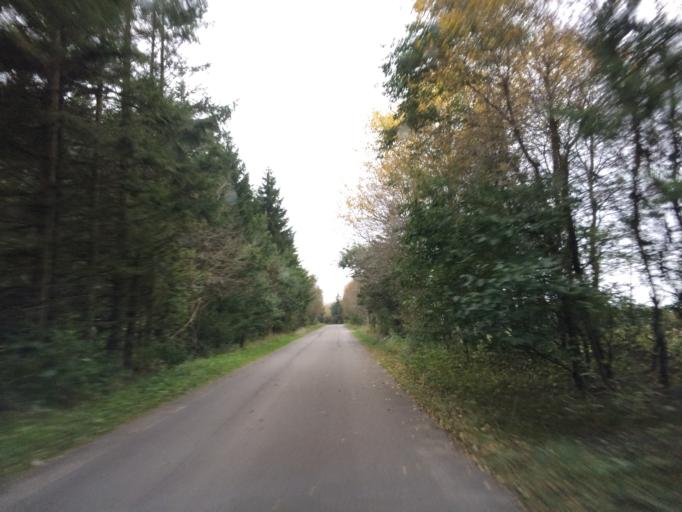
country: DK
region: Central Jutland
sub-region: Holstebro Kommune
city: Ulfborg
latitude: 56.2366
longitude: 8.4222
